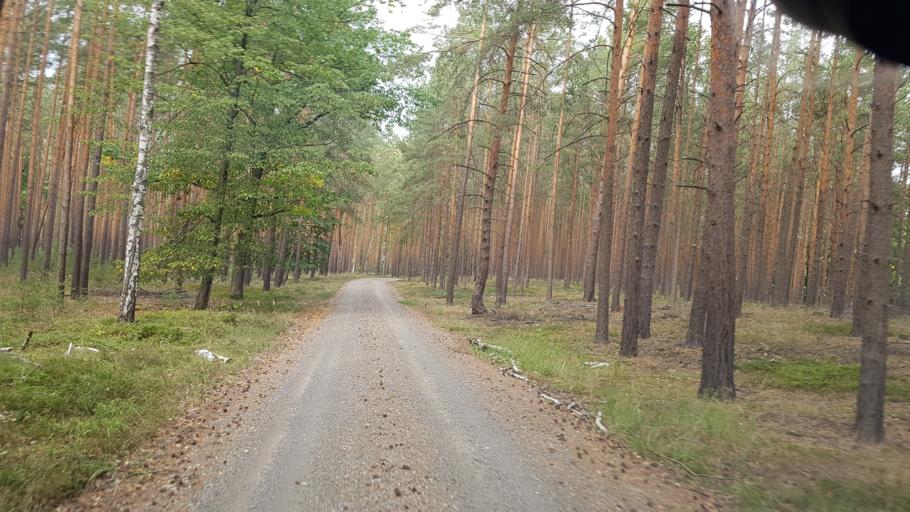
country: DE
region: Brandenburg
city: Ruckersdorf
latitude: 51.5745
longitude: 13.6103
